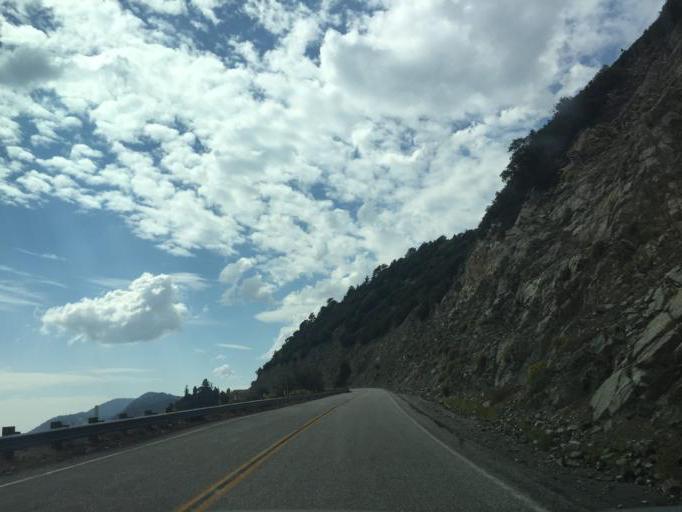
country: US
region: California
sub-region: Los Angeles County
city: Littlerock
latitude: 34.3568
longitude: -117.8523
